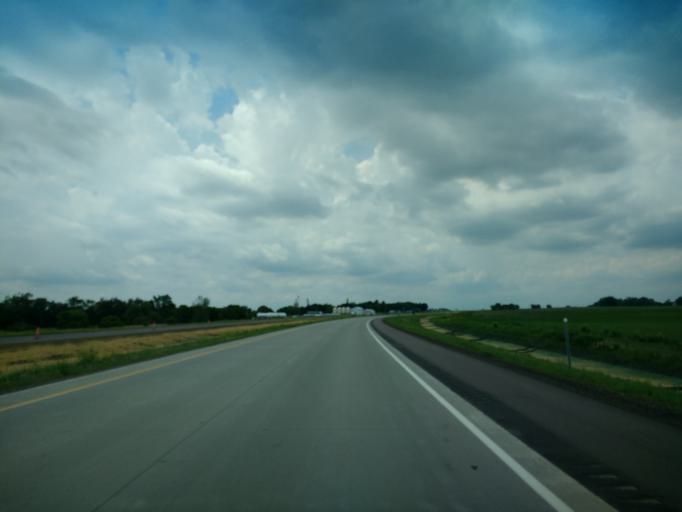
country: US
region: Minnesota
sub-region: Cottonwood County
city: Windom
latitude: 43.9108
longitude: -95.0292
